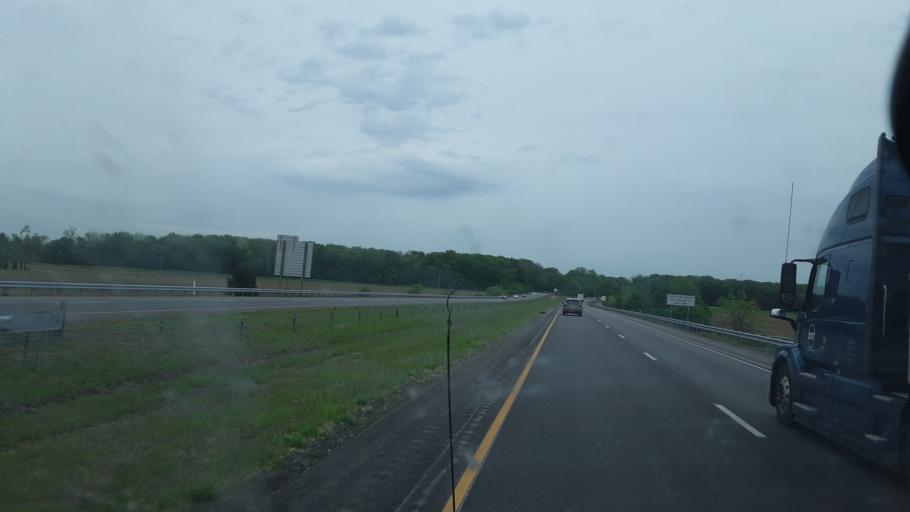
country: US
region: Indiana
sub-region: Gibson County
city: Haubstadt
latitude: 38.1653
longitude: -87.6688
